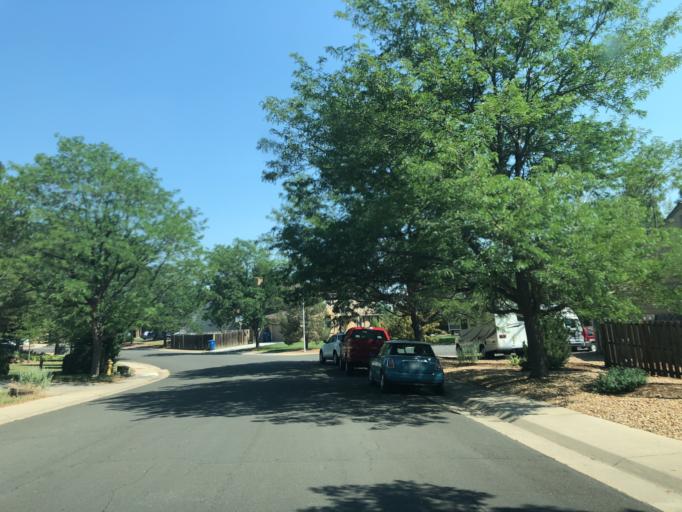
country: US
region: Colorado
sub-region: Arapahoe County
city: Dove Valley
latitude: 39.6348
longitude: -104.7652
